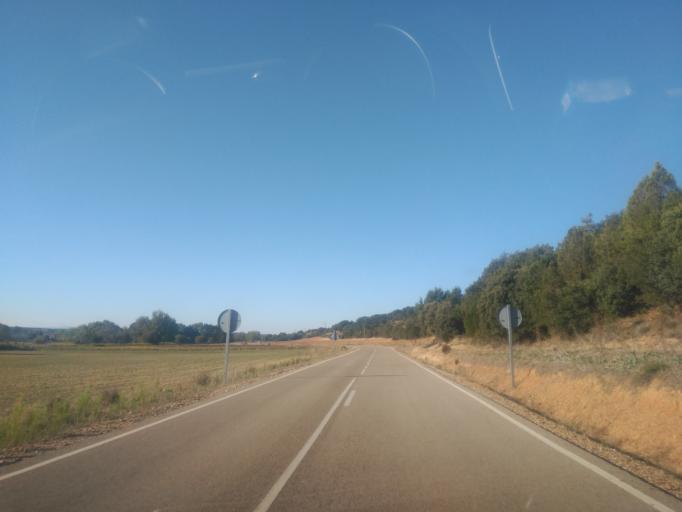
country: ES
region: Castille and Leon
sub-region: Provincia de Soria
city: Alcubilla de Avellaneda
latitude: 41.7417
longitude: -3.2915
